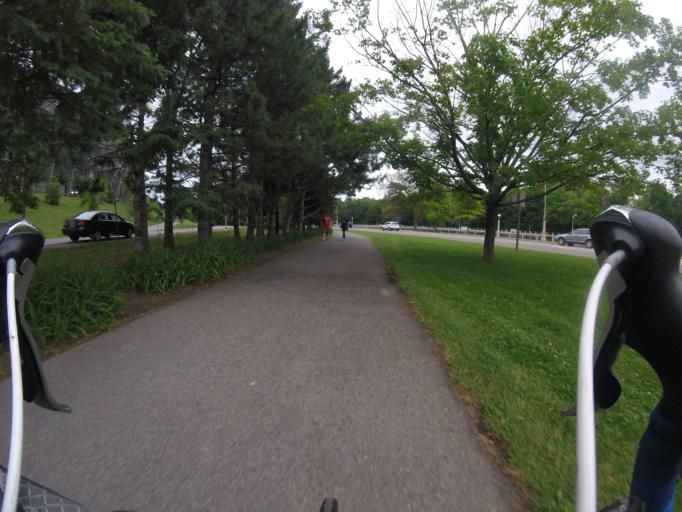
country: CA
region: Ontario
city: Ottawa
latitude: 45.3970
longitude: -75.6842
